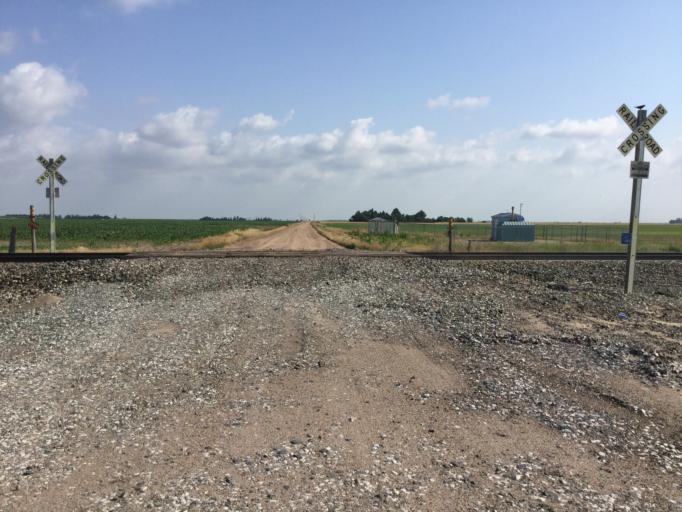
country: US
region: Kansas
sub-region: Pawnee County
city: Larned
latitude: 37.9560
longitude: -99.0588
